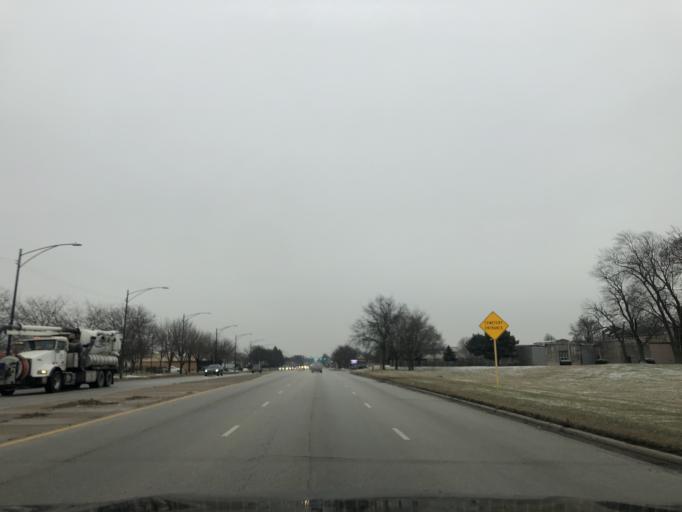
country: US
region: Illinois
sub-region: Cook County
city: Evergreen Park
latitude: 41.7351
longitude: -87.7066
